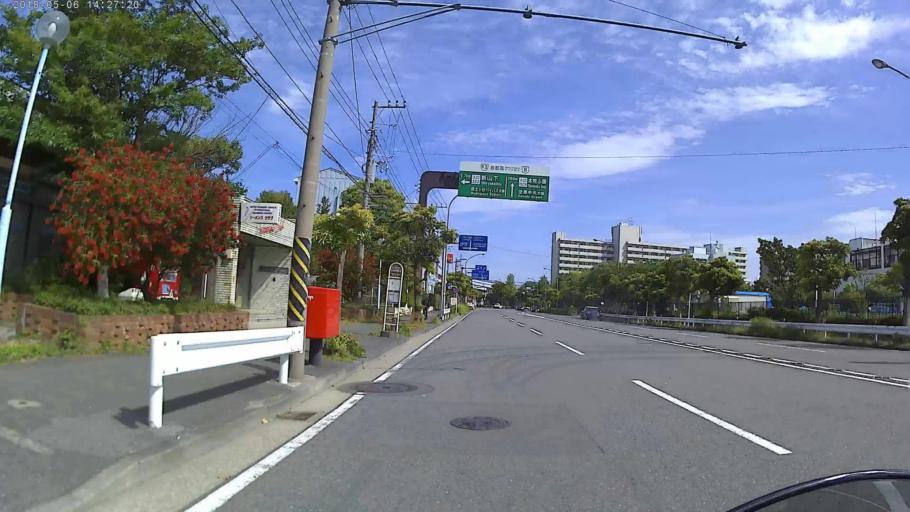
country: JP
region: Kanagawa
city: Yokohama
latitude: 35.4330
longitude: 139.6677
